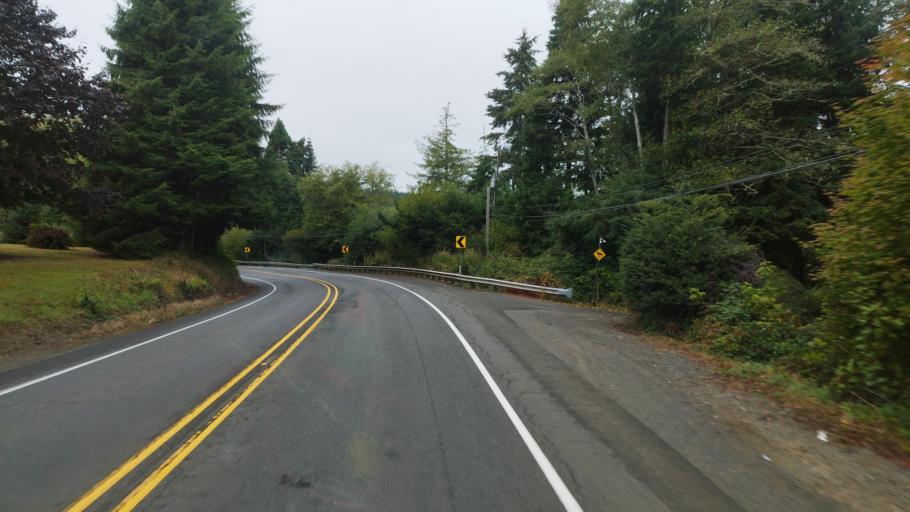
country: US
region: Oregon
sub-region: Clatsop County
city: Astoria
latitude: 46.1700
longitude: -123.7283
